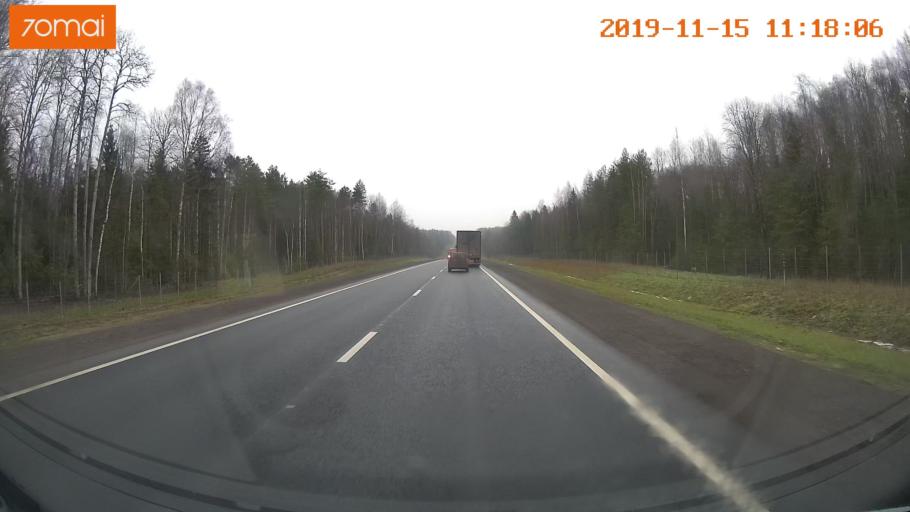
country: RU
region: Vologda
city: Chebsara
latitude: 59.1349
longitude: 39.2648
